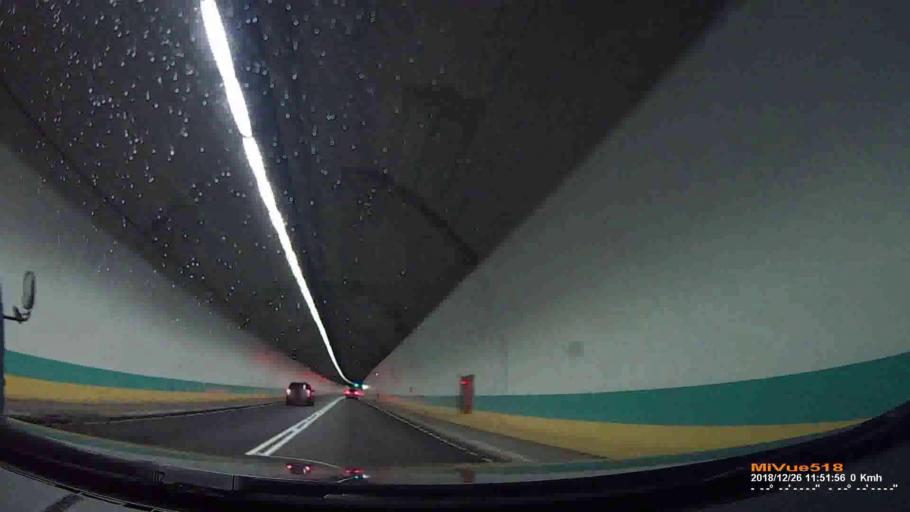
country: TW
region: Taipei
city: Taipei
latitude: 24.9710
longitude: 121.6807
